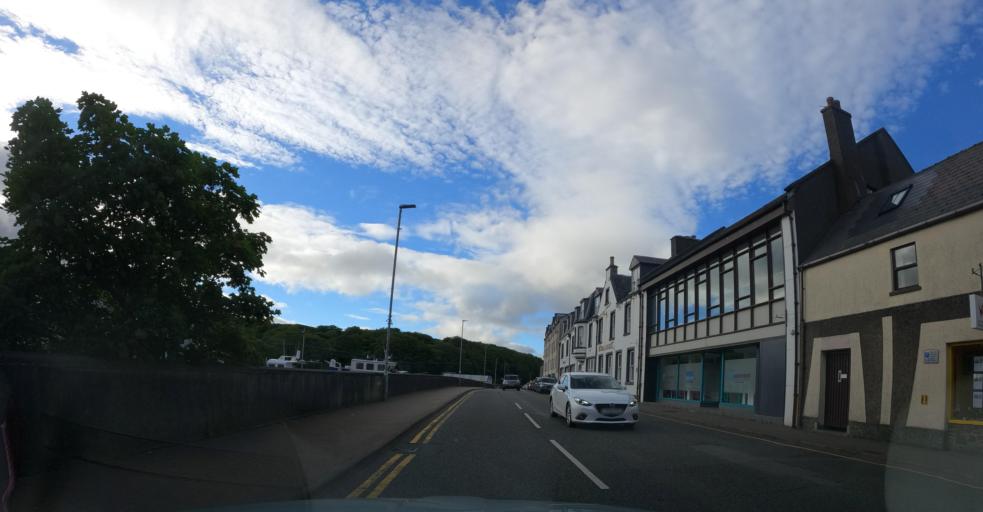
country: GB
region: Scotland
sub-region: Eilean Siar
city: Stornoway
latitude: 58.2102
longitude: -6.3887
